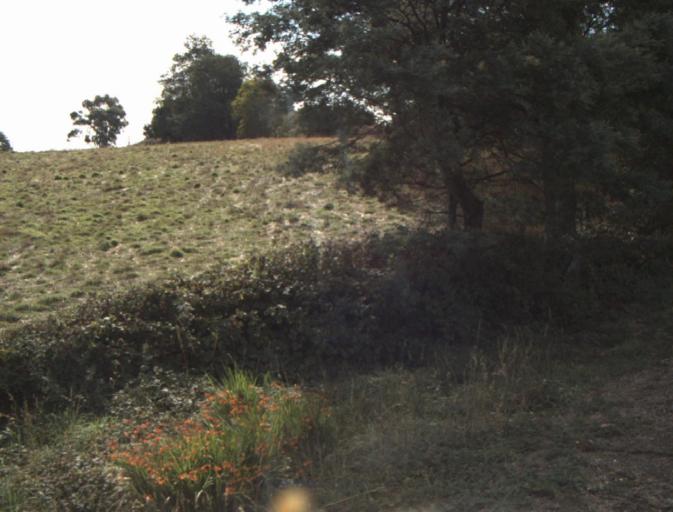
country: AU
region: Tasmania
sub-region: Launceston
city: Mayfield
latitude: -41.1943
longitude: 147.1951
